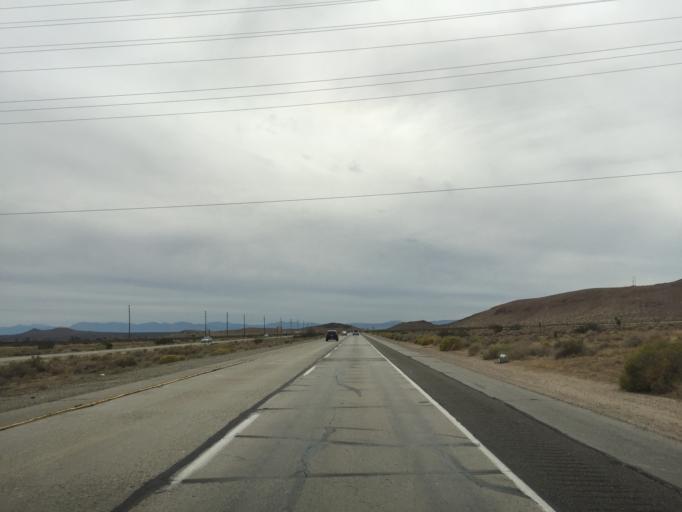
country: US
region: California
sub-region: Kern County
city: Mojave
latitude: 34.9955
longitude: -118.1600
